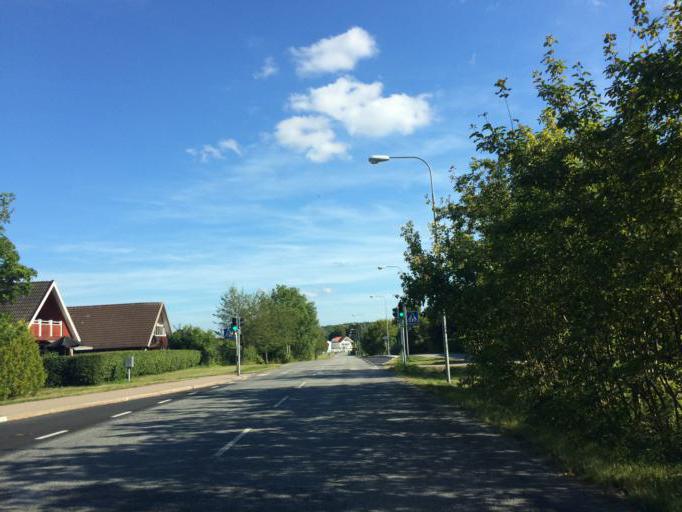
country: SE
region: Stockholm
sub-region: Upplands Vasby Kommun
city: Upplands Vaesby
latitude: 59.4940
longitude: 17.9428
